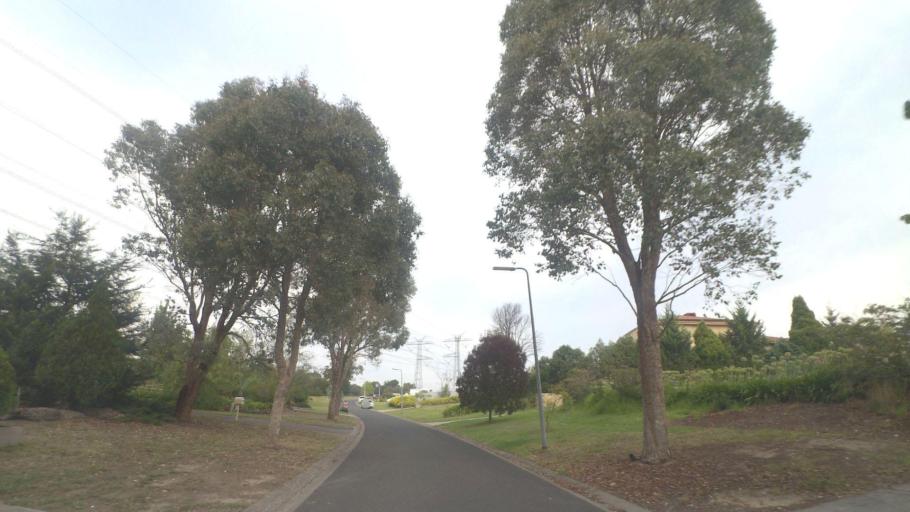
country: AU
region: Victoria
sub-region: Manningham
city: Donvale
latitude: -37.7642
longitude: 145.1878
